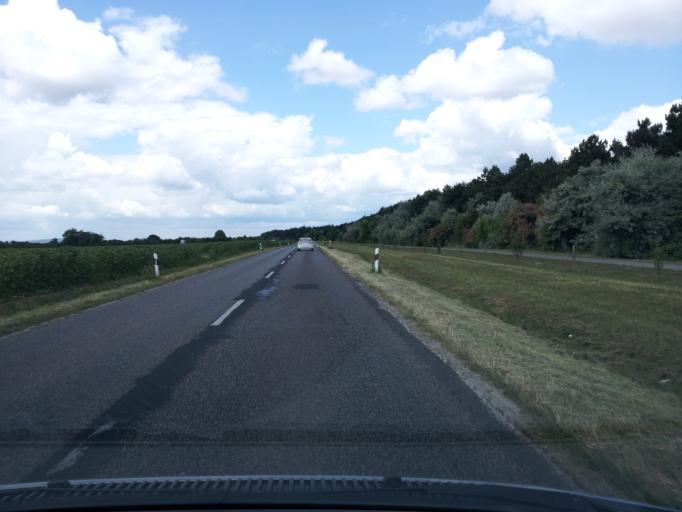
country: HU
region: Veszprem
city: Szentkiralyszabadja
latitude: 47.0694
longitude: 17.9471
